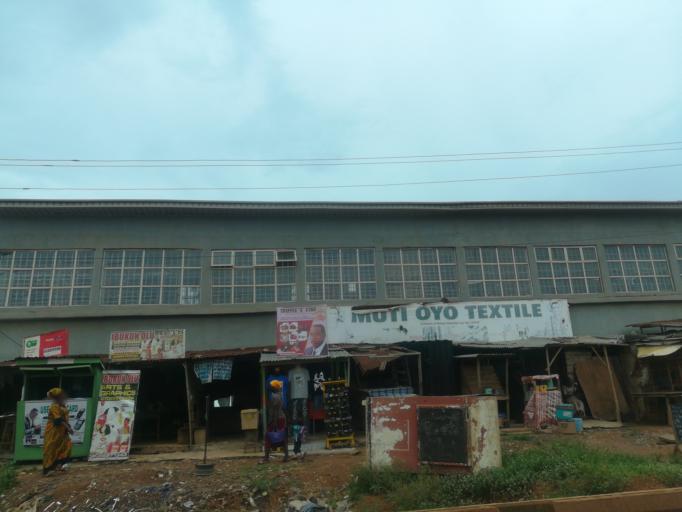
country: NG
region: Oyo
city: Ibadan
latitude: 7.3905
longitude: 3.9572
